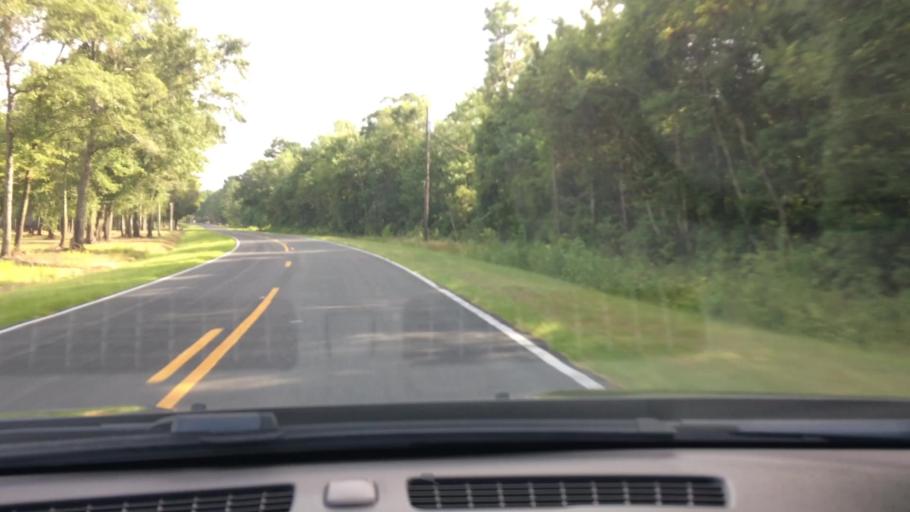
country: US
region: North Carolina
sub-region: Beaufort County
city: Washington
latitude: 35.4436
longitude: -77.1226
